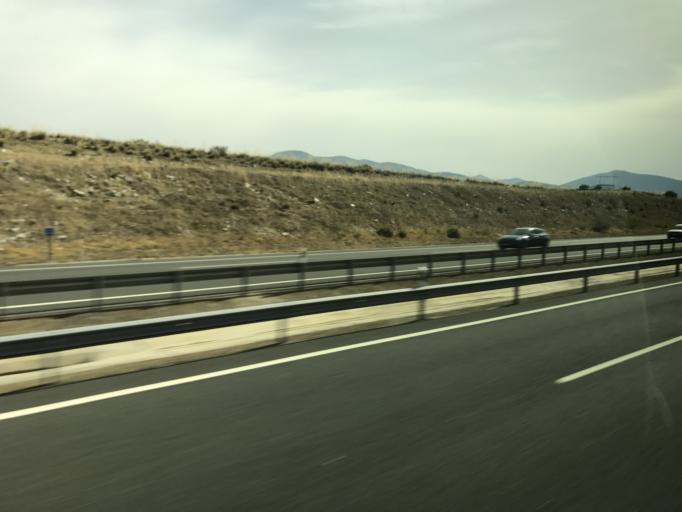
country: ES
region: Castille and Leon
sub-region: Provincia de Segovia
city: Vegas de Matute
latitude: 40.7388
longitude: -4.2367
